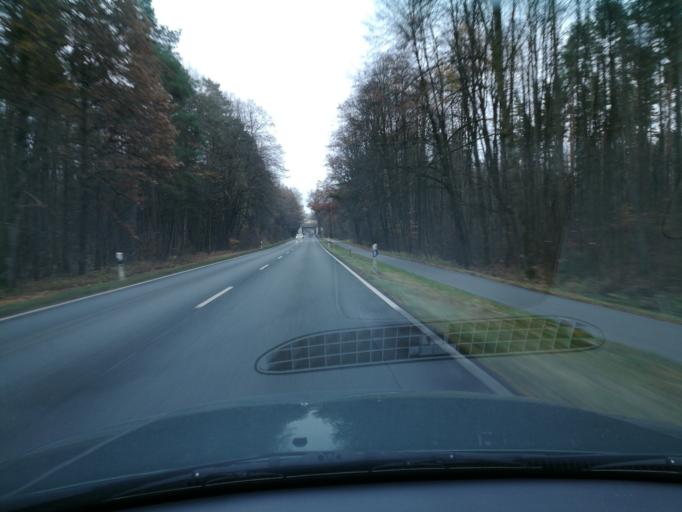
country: DE
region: Bavaria
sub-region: Regierungsbezirk Mittelfranken
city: Feucht
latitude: 49.3870
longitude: 11.1969
